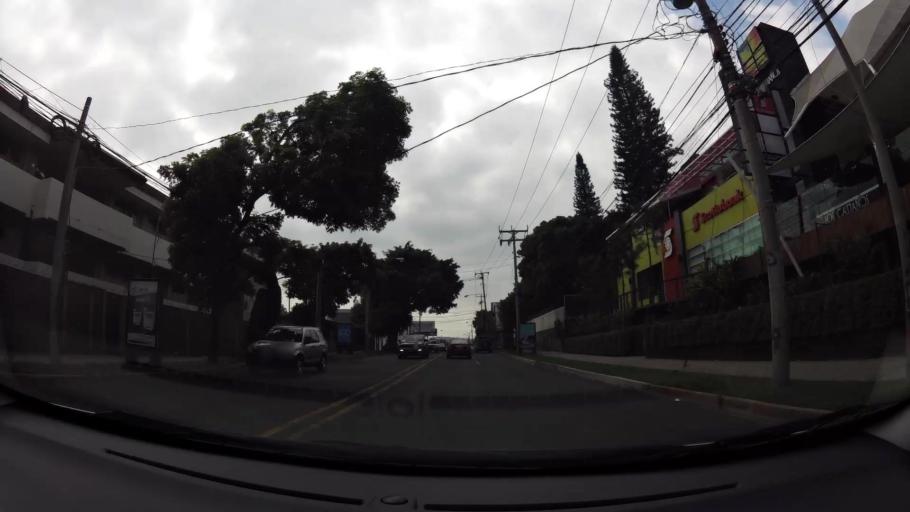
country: SV
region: La Libertad
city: Antiguo Cuscatlan
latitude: 13.7095
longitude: -89.2484
